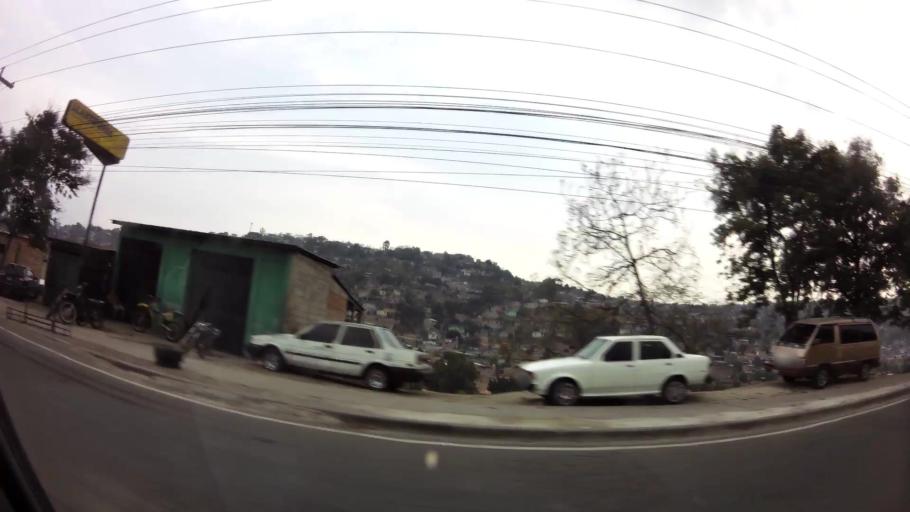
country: HN
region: Francisco Morazan
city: Tegucigalpa
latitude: 14.0868
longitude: -87.2324
